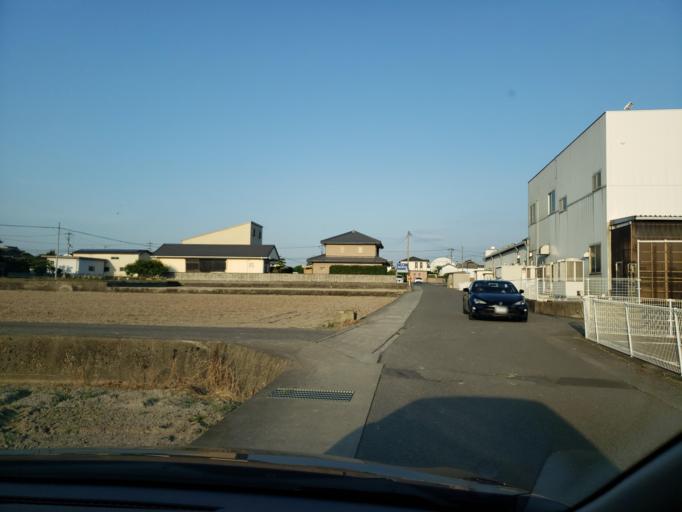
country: JP
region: Tokushima
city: Wakimachi
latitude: 34.0757
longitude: 134.2340
